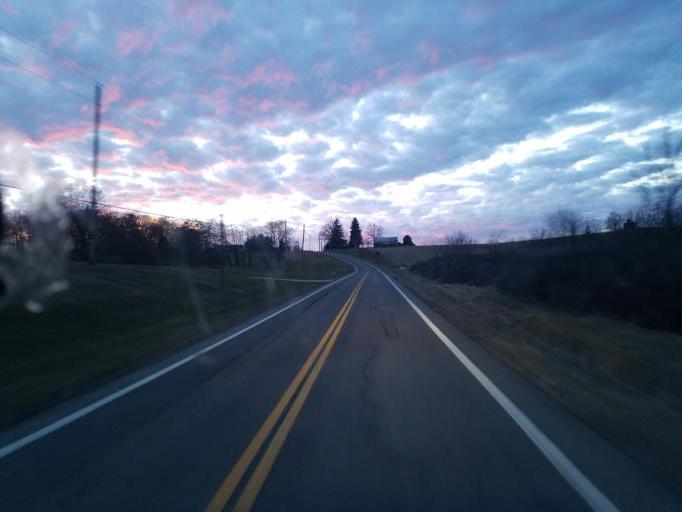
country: US
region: Ohio
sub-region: Knox County
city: Oak Hill
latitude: 40.2861
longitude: -82.2537
